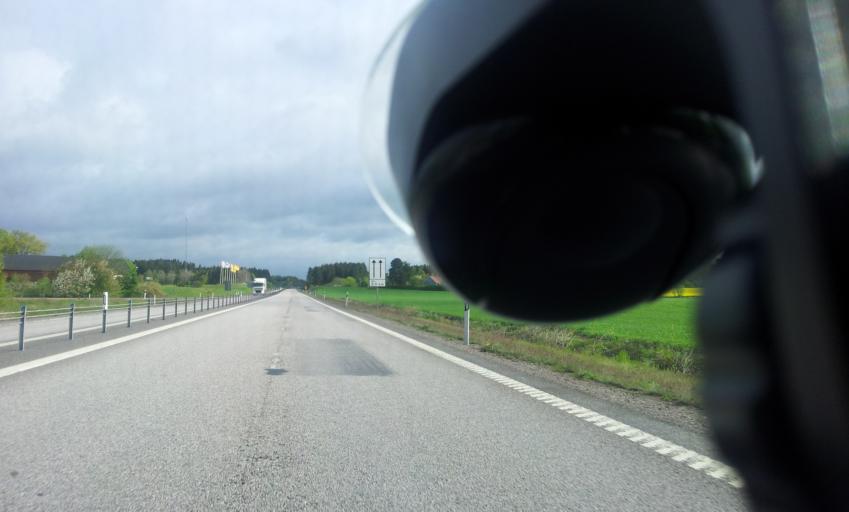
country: SE
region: Kalmar
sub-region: Torsas Kommun
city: Torsas
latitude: 56.4525
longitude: 16.0788
